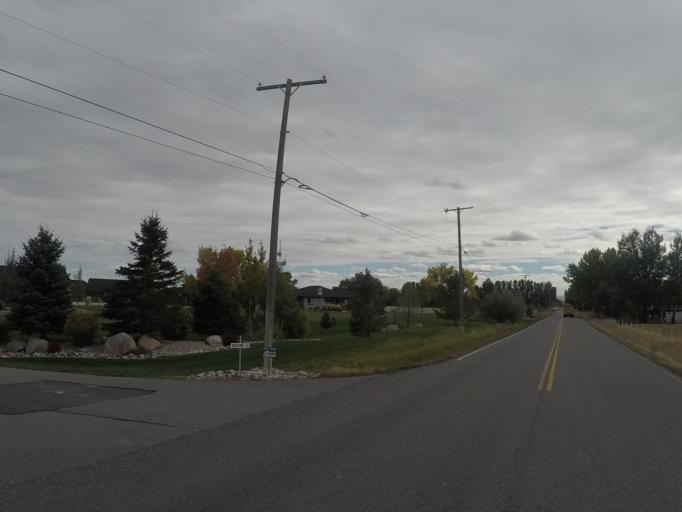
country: US
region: Montana
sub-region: Yellowstone County
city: Laurel
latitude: 45.7390
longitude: -108.6588
